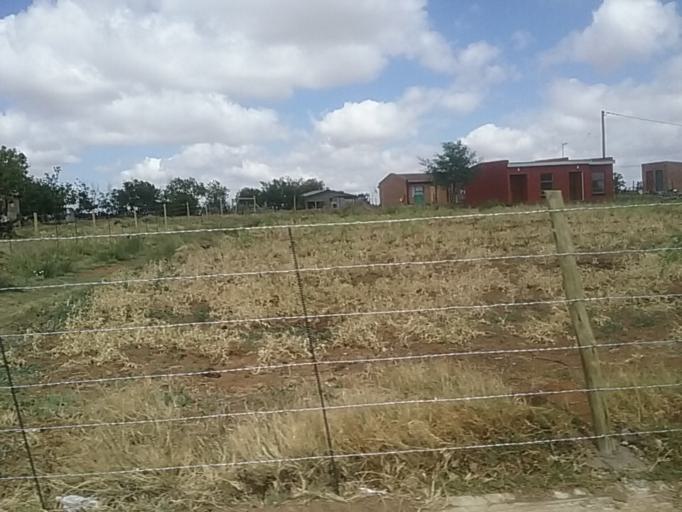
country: LS
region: Berea
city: Teyateyaneng
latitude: -29.1365
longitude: 27.7343
